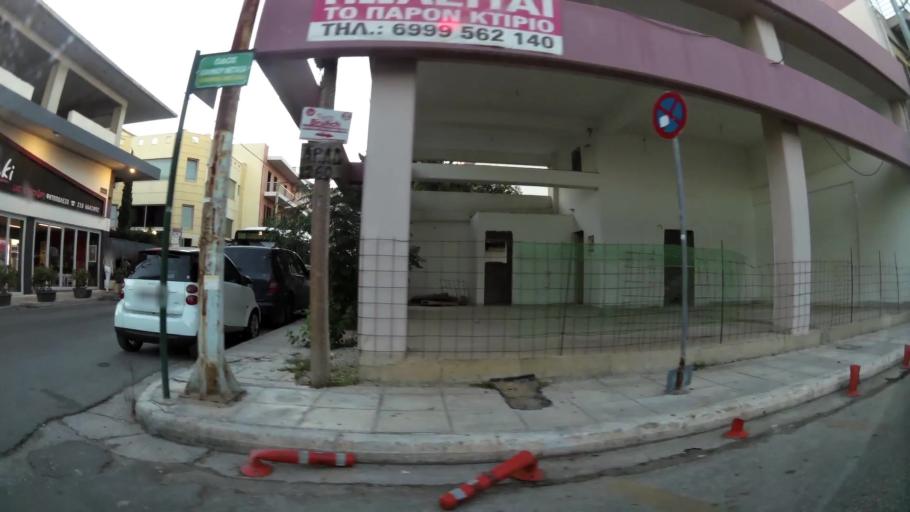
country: GR
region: Attica
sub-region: Nomarchia Anatolikis Attikis
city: Paiania
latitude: 37.9556
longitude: 23.8541
